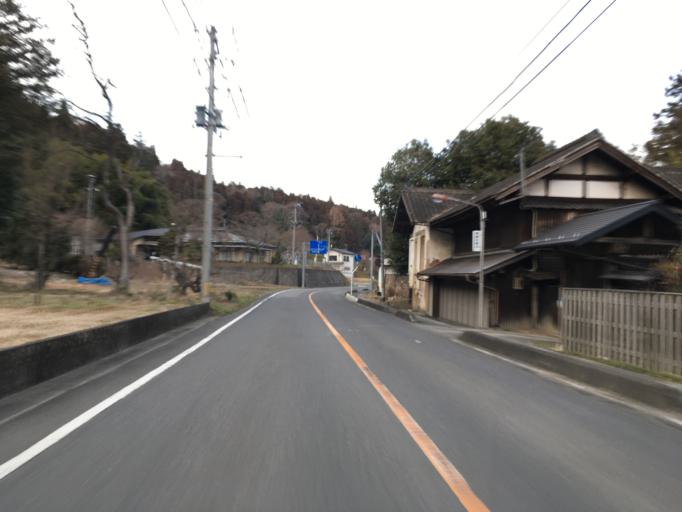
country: JP
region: Ibaraki
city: Daigo
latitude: 36.9032
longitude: 140.4065
